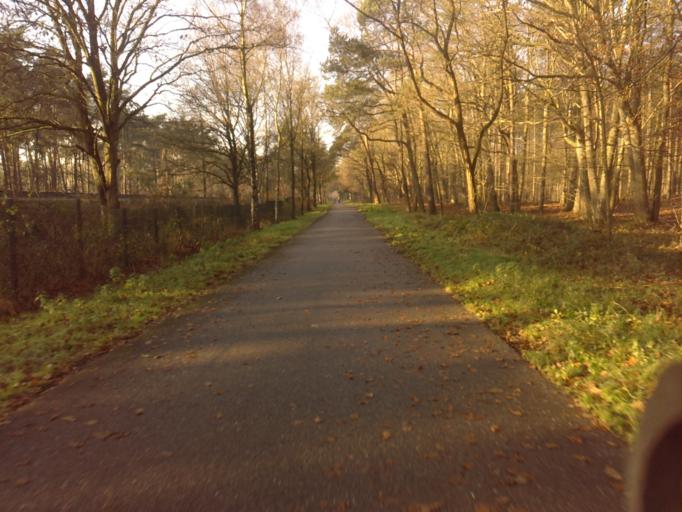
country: NL
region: Utrecht
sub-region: Gemeente Soest
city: Soest
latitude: 52.1448
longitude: 5.3090
